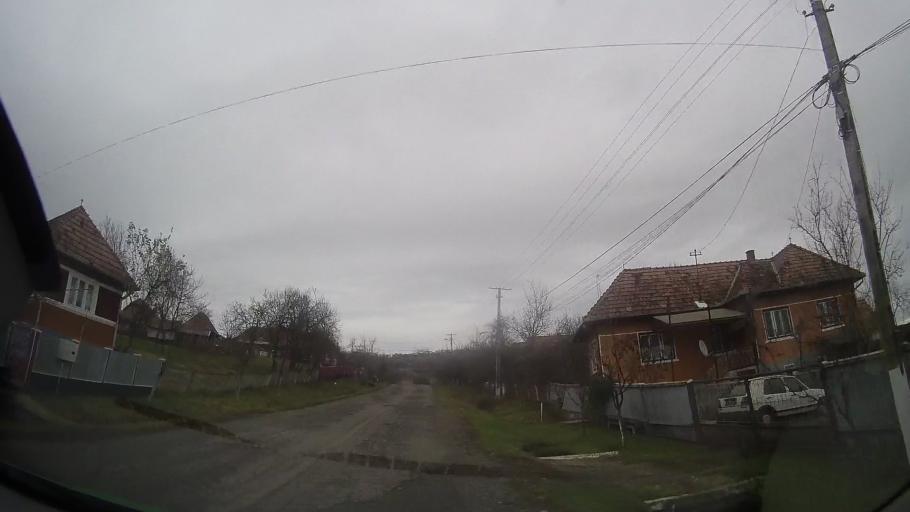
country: RO
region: Mures
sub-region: Comuna Bala
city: Bala
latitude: 46.7102
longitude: 24.5016
